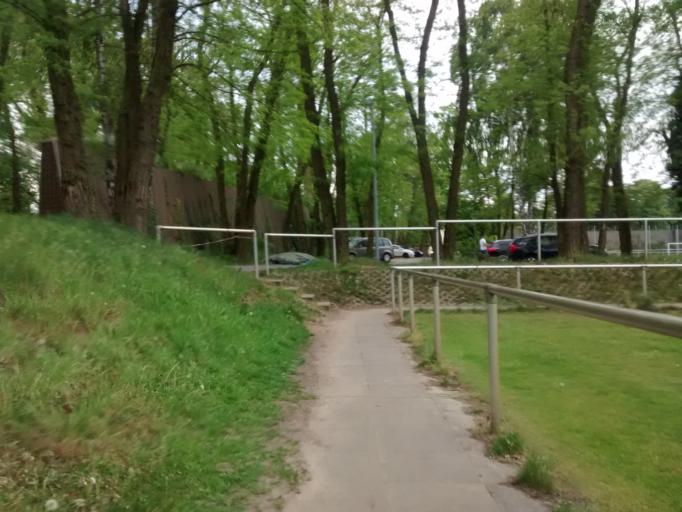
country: DE
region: Brandenburg
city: Hohen Neuendorf
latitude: 52.6778
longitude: 13.2618
